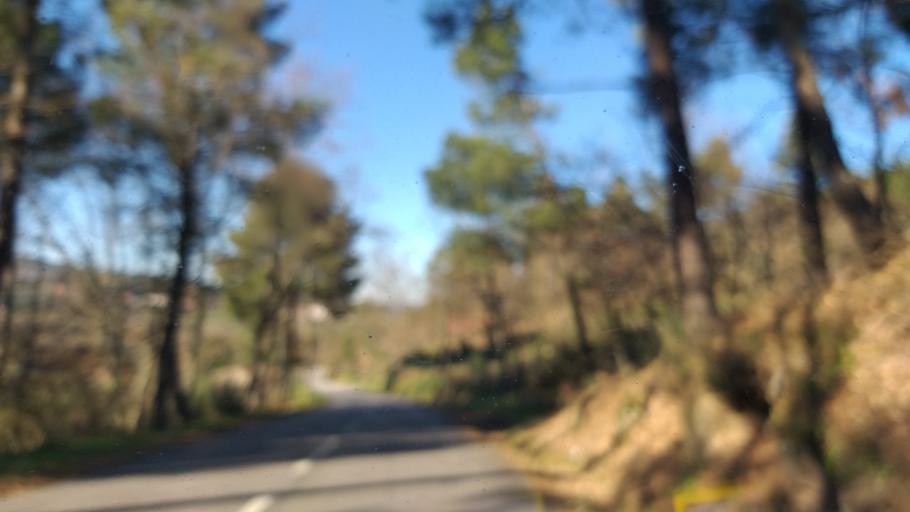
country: PT
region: Guarda
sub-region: Celorico da Beira
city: Celorico da Beira
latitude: 40.5932
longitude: -7.3625
